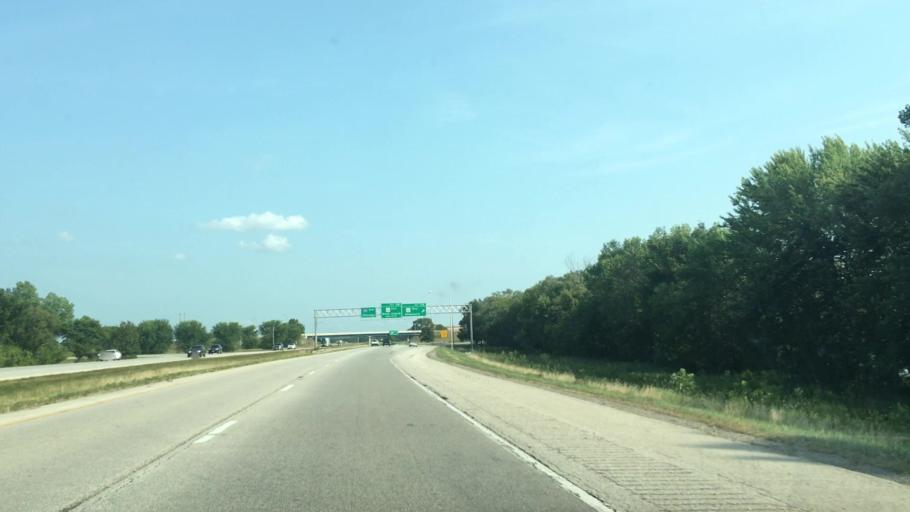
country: US
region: Illinois
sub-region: Rock Island County
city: Milan
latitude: 41.4683
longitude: -90.6188
